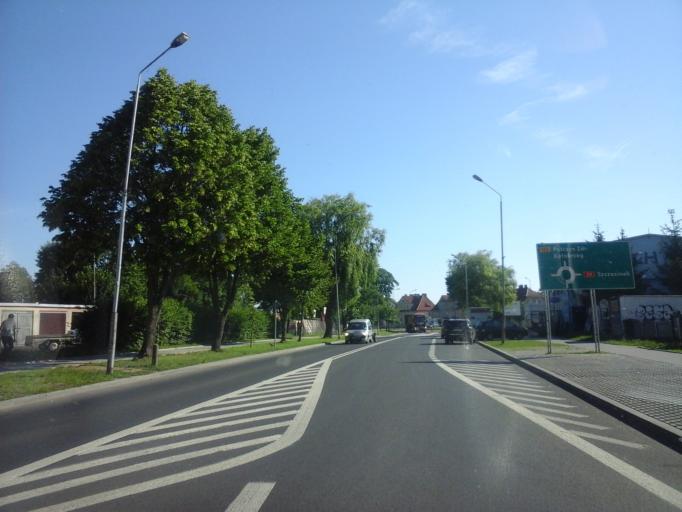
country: PL
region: West Pomeranian Voivodeship
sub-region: Powiat drawski
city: Drawsko Pomorskie
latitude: 53.5362
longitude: 15.8113
